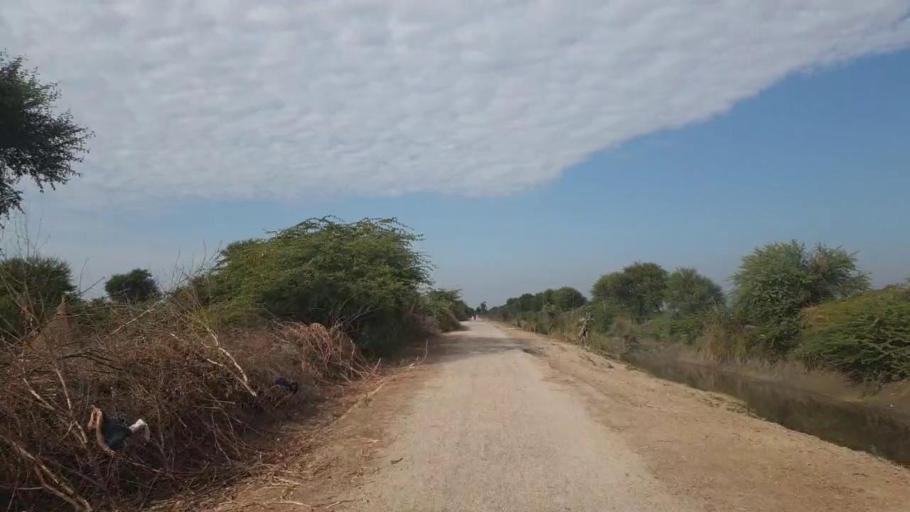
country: PK
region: Sindh
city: Sinjhoro
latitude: 26.0624
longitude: 68.8733
